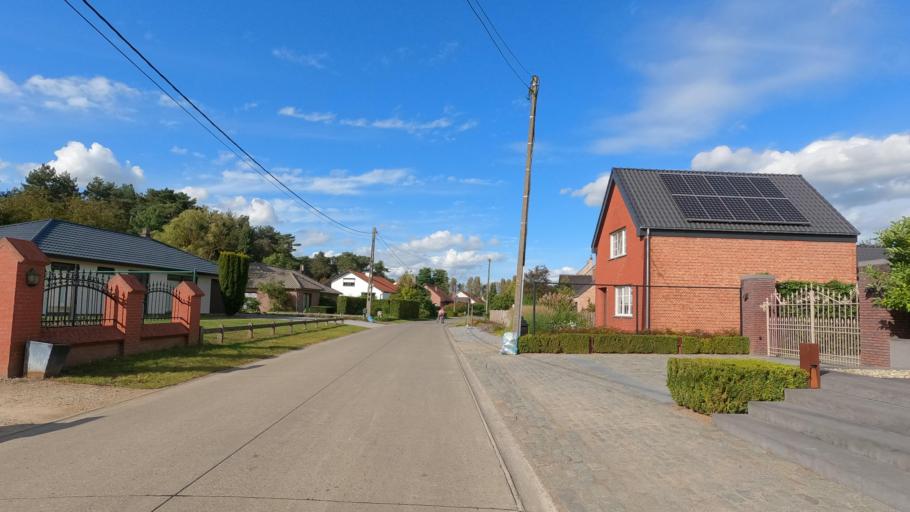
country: BE
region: Flanders
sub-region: Provincie Antwerpen
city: Herselt
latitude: 51.0198
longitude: 4.9159
